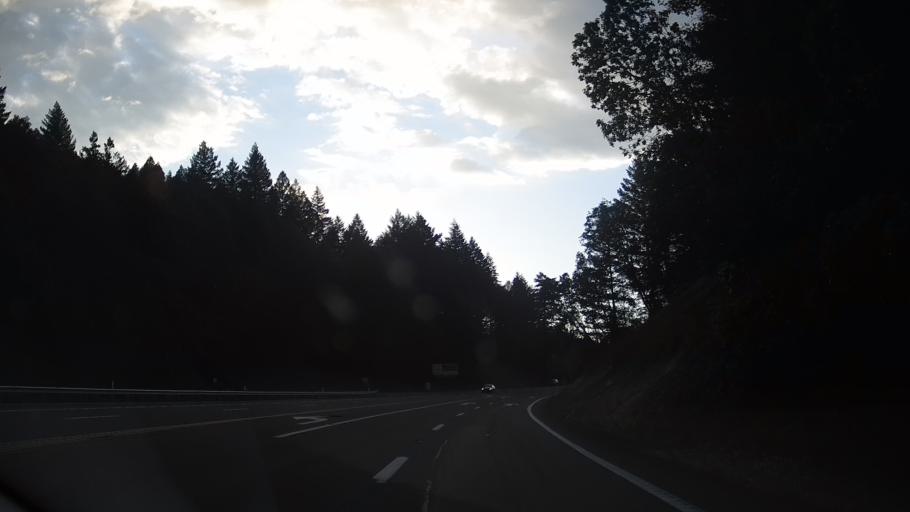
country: US
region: California
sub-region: Mendocino County
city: Willits
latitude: 39.3381
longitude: -123.3110
